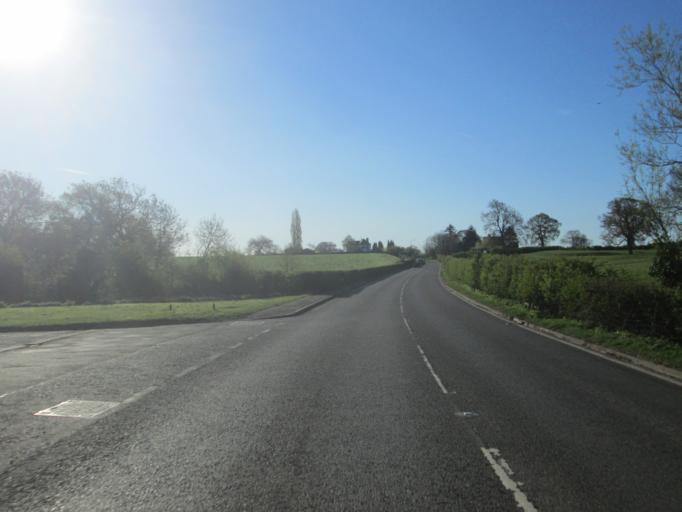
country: GB
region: England
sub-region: Derbyshire
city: Findern
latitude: 52.9393
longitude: -1.5461
